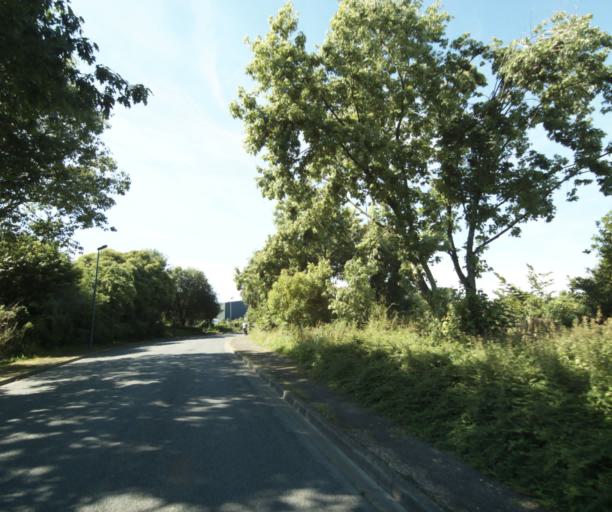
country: FR
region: Pays de la Loire
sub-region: Departement de la Mayenne
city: Laval
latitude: 48.0569
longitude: -0.7978
